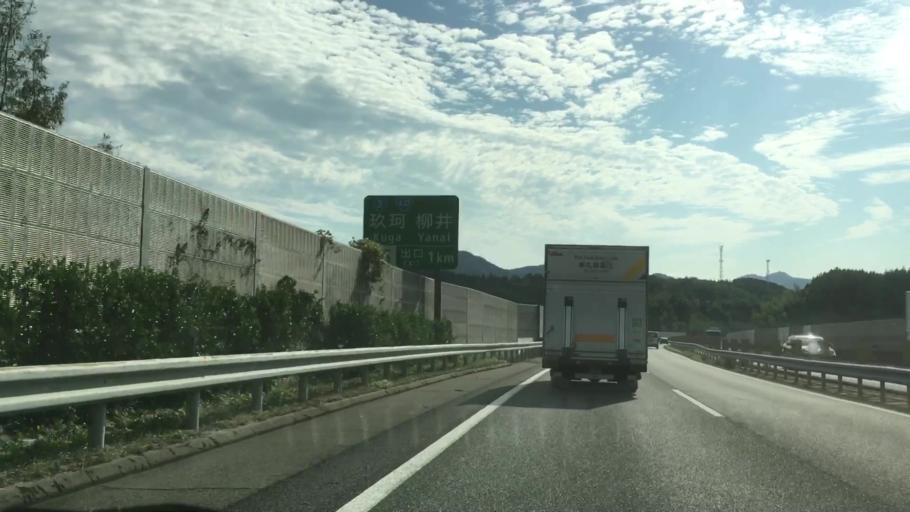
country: JP
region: Yamaguchi
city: Yanai
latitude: 34.0892
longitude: 132.0937
